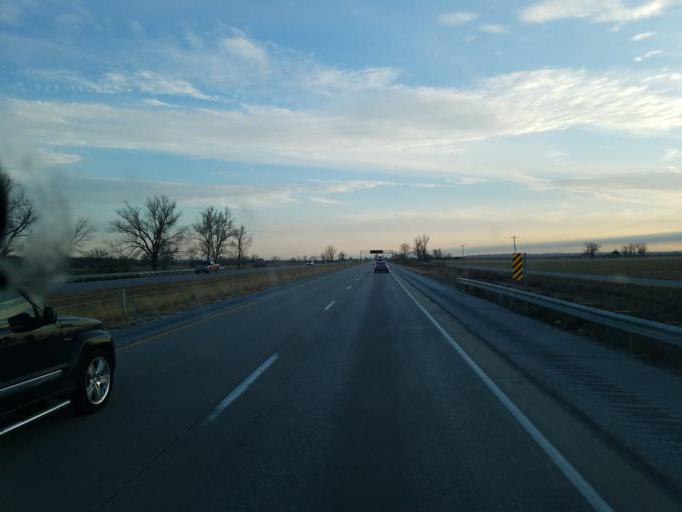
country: US
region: Iowa
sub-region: Harrison County
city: Missouri Valley
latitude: 41.5276
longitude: -95.9179
